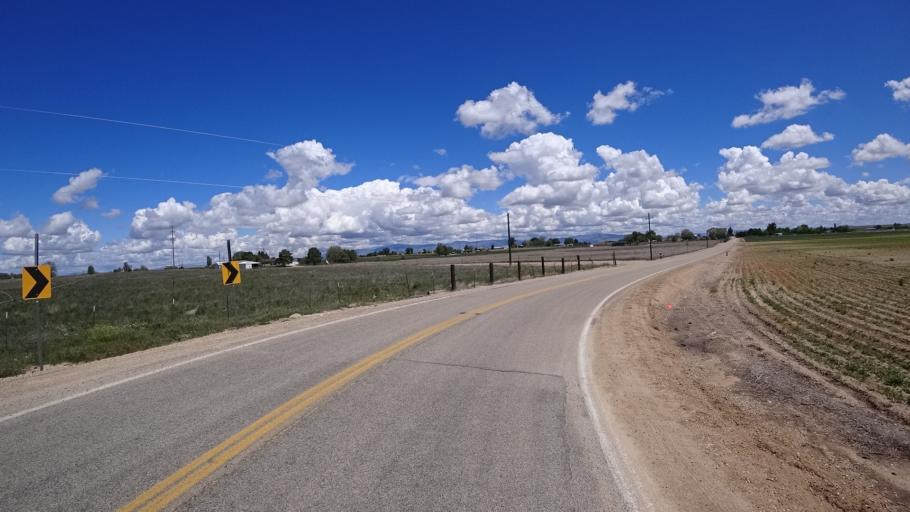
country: US
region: Idaho
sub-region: Ada County
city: Kuna
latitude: 43.5245
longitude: -116.3629
